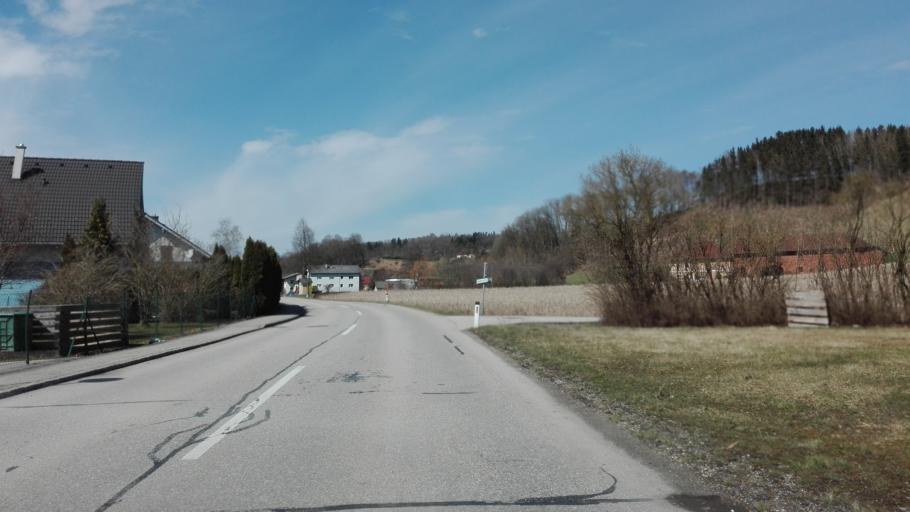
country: AT
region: Upper Austria
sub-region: Politischer Bezirk Grieskirchen
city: Grieskirchen
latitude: 48.2382
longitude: 13.8105
